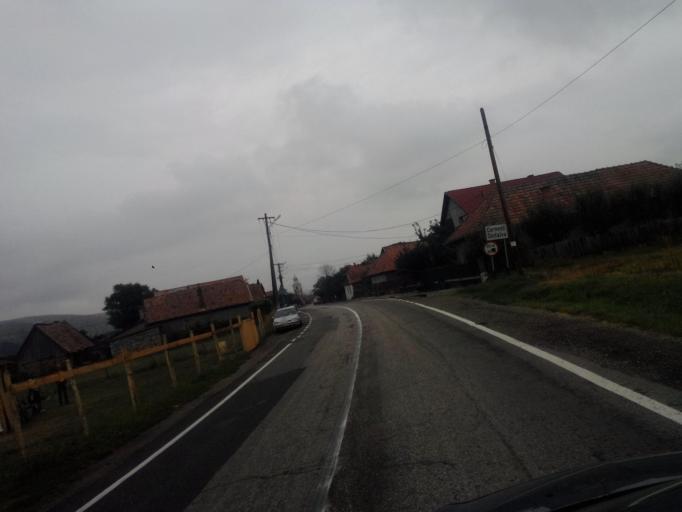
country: RO
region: Cluj
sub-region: Comuna Moldovenesti
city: Moldovenesti
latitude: 46.5186
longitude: 23.6827
